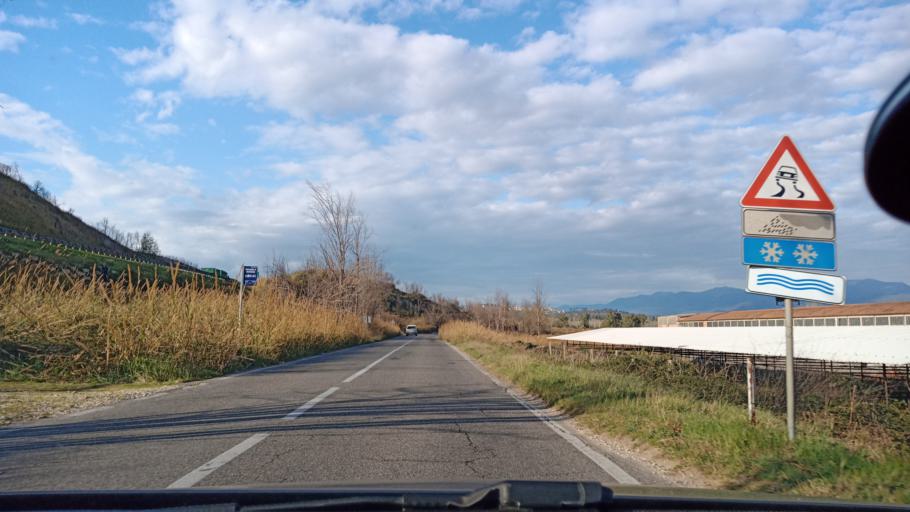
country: IT
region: Latium
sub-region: Citta metropolitana di Roma Capitale
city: Civitella San Paolo
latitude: 42.1937
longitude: 12.6046
